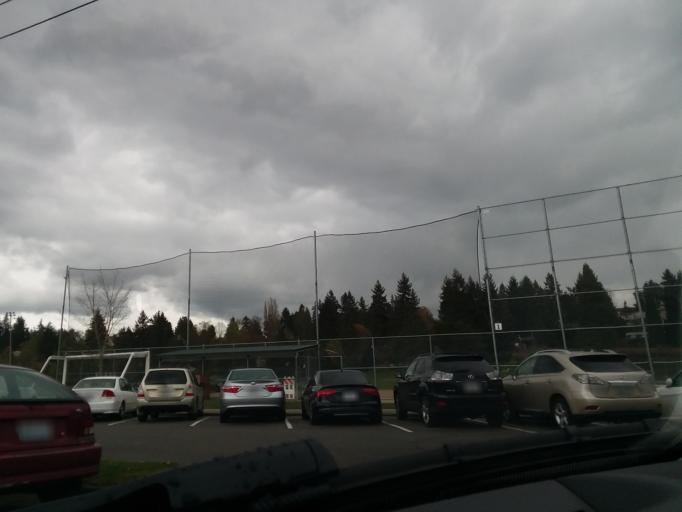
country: US
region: Washington
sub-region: King County
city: Lake Forest Park
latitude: 47.6851
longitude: -122.3008
